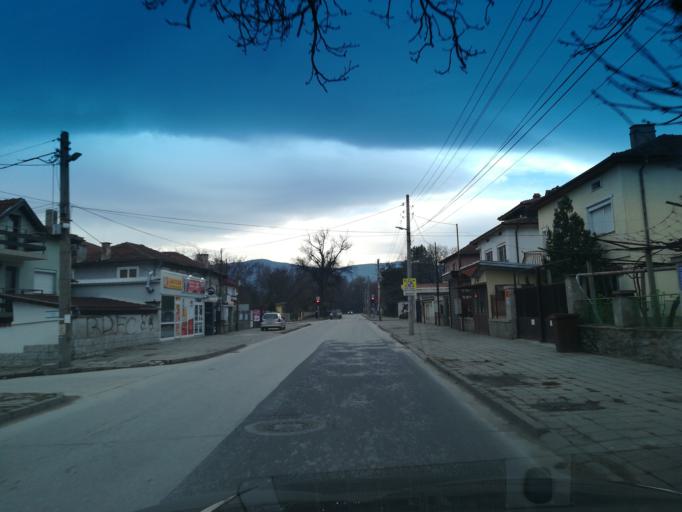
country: BG
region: Plovdiv
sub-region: Obshtina Plovdiv
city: Plovdiv
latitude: 42.1033
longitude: 24.7041
